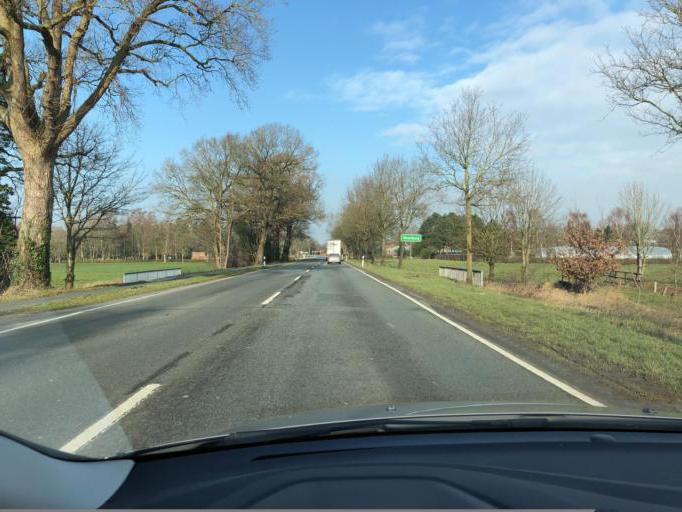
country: DE
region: Lower Saxony
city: Westerstede
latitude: 53.2832
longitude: 7.8991
